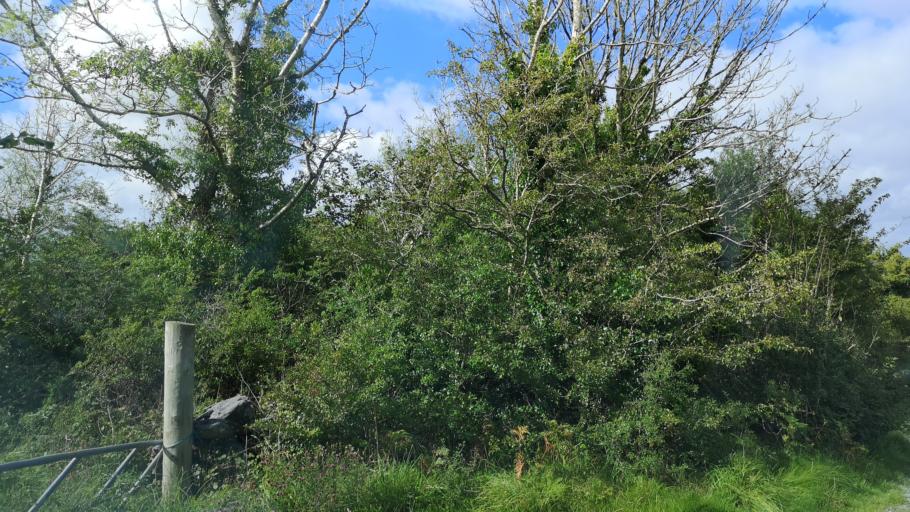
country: IE
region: Connaught
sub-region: County Galway
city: Moycullen
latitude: 53.3575
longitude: -9.1563
